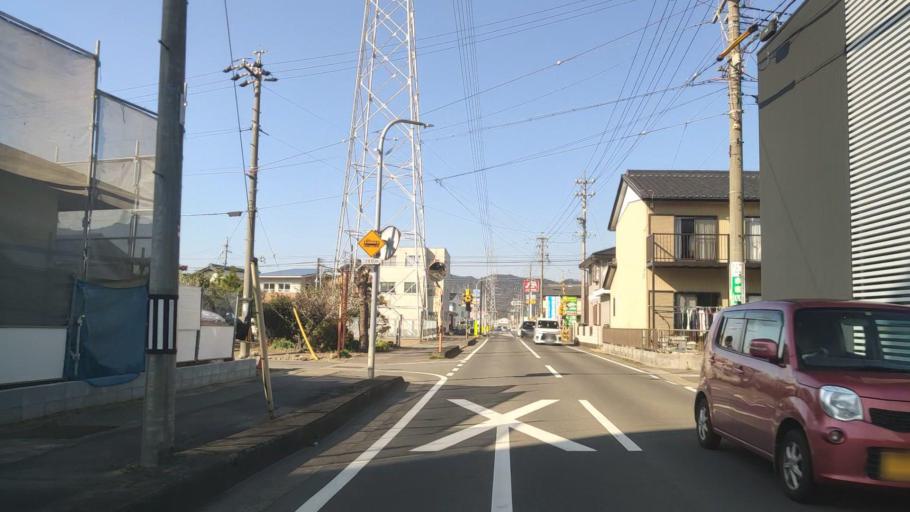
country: JP
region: Gifu
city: Gifu-shi
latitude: 35.4007
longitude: 136.7910
